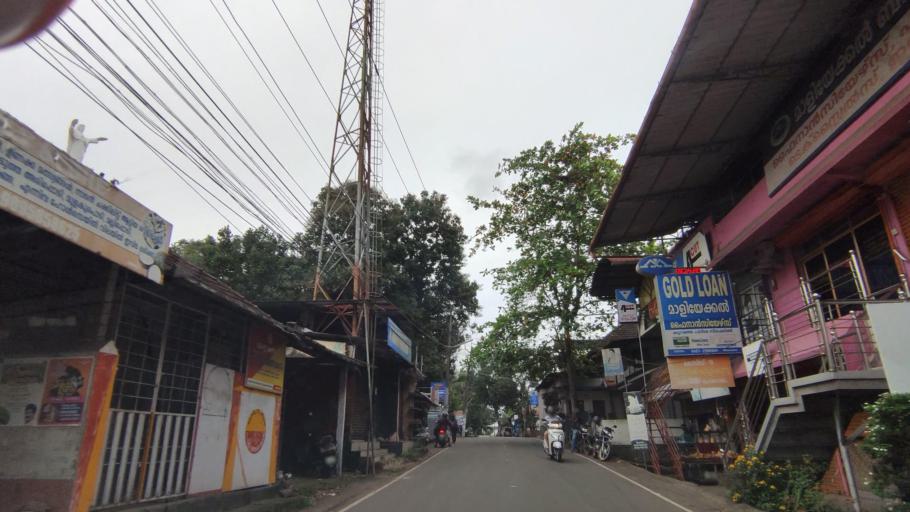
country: IN
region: Kerala
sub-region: Kottayam
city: Kottayam
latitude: 9.6491
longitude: 76.5210
